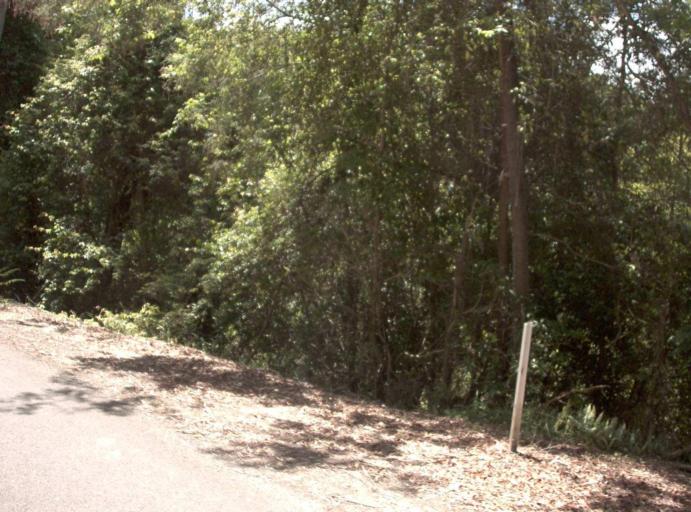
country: AU
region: New South Wales
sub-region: Bombala
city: Bombala
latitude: -37.4770
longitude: 148.9261
